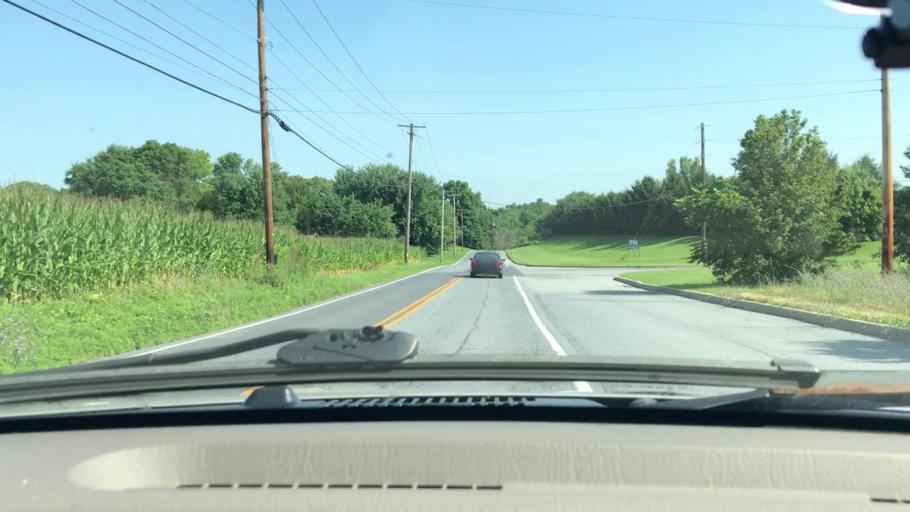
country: US
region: Pennsylvania
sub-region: Dauphin County
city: Middletown
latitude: 40.2343
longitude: -76.7377
